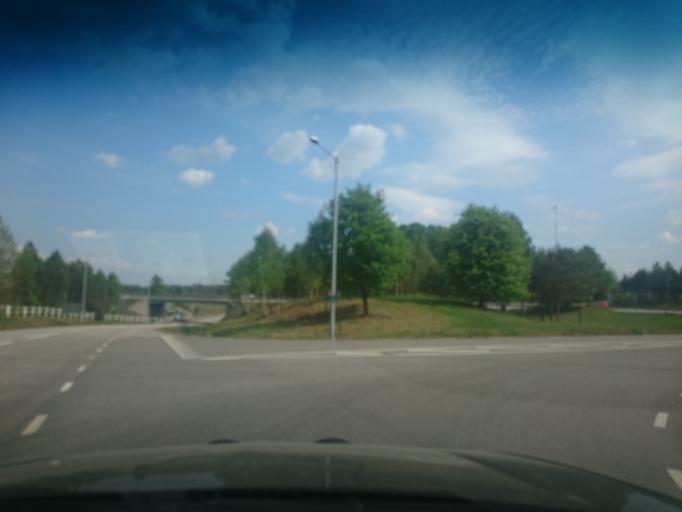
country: SE
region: Joenkoeping
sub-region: Vetlanda Kommun
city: Vetlanda
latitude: 57.4198
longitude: 15.1090
